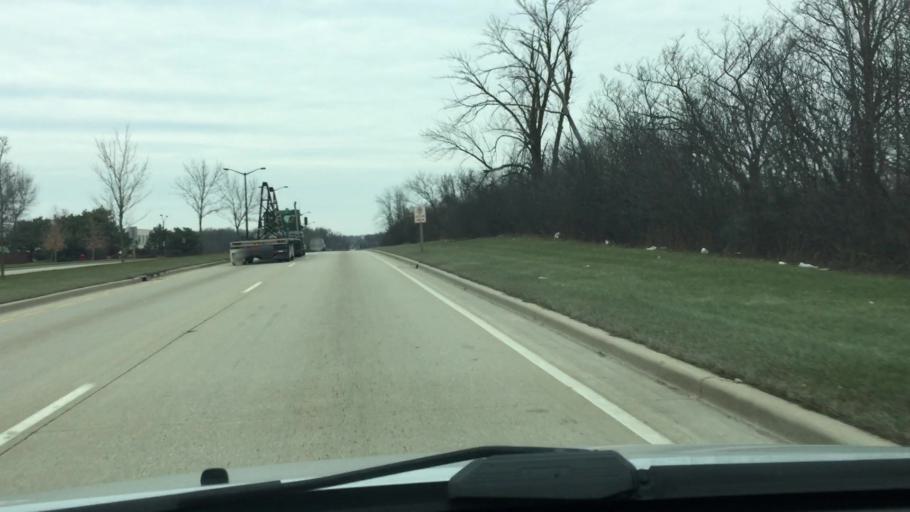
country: US
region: Wisconsin
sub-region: Waukesha County
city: Menomonee Falls
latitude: 43.1709
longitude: -88.0640
